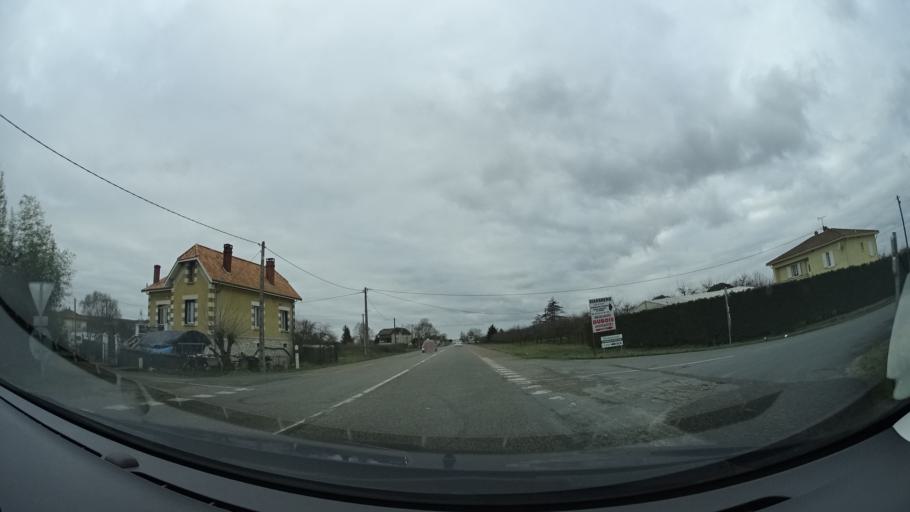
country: FR
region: Aquitaine
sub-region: Departement du Lot-et-Garonne
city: Bias
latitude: 44.4026
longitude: 0.6598
